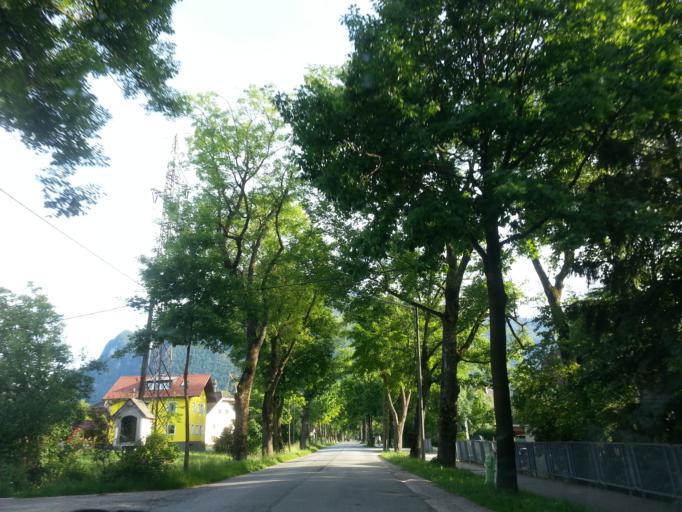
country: AT
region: Salzburg
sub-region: Politischer Bezirk Salzburg-Umgebung
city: Grodig
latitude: 47.7632
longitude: 13.0176
